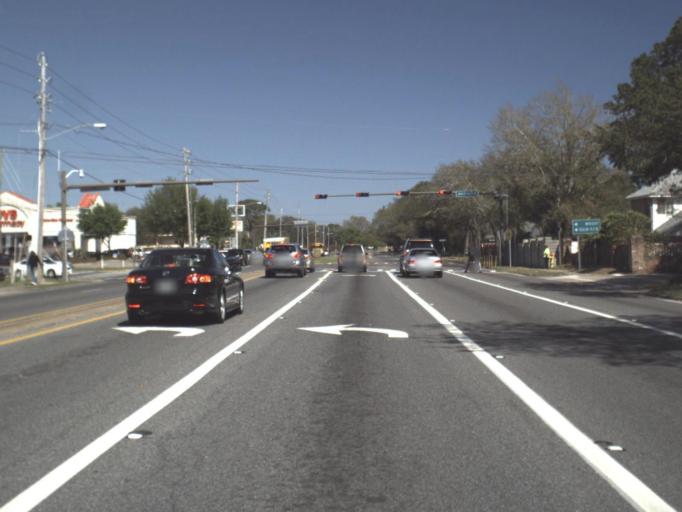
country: US
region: Florida
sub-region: Okaloosa County
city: Mary Esther
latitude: 30.4094
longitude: -86.6566
